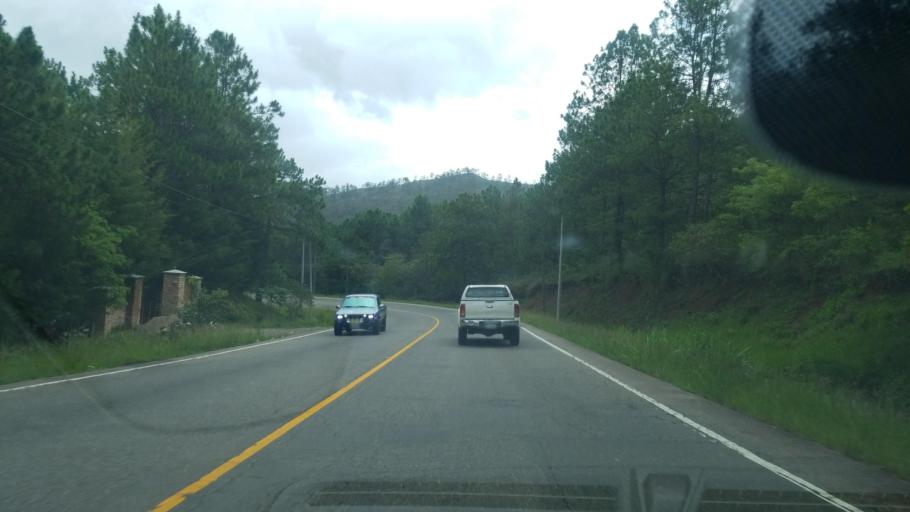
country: HN
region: Ocotepeque
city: Sinuapa
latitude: 14.4603
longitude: -89.1579
